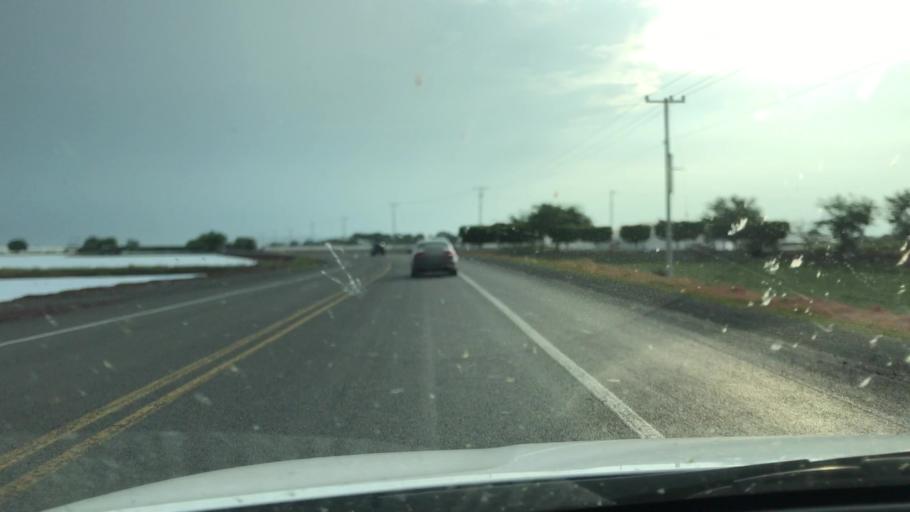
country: MX
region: Michoacan
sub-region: Yurecuaro
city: Yurecuaro
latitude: 20.3220
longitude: -102.2871
